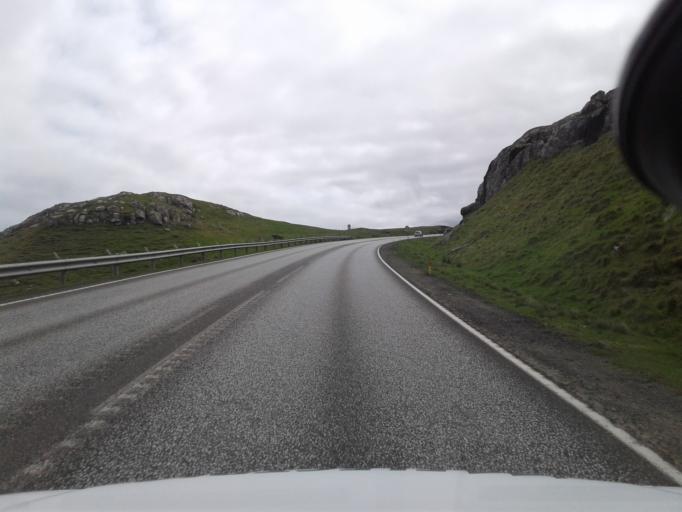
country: FO
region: Streymoy
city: Hoyvik
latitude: 62.0485
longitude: -6.7875
